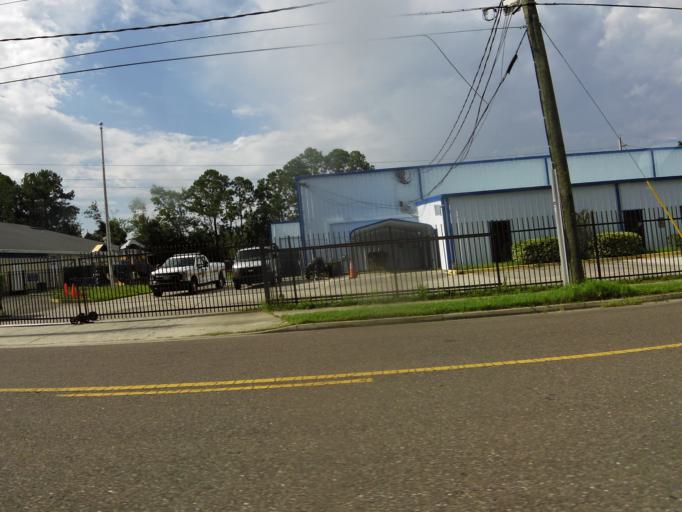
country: US
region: Florida
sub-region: Duval County
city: Jacksonville
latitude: 30.3647
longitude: -81.6966
